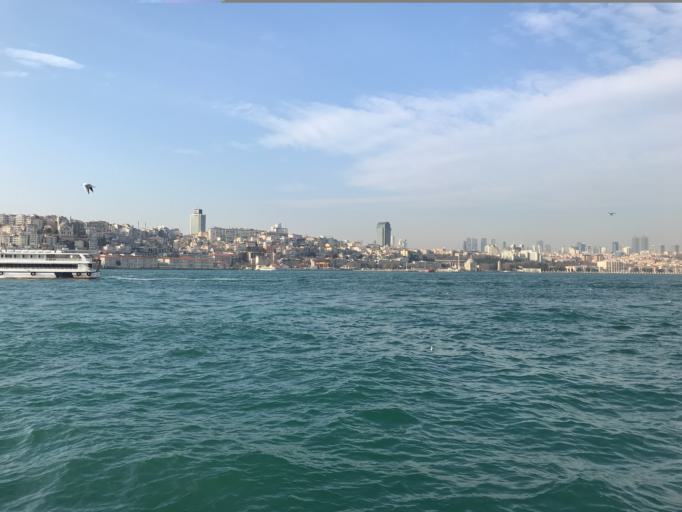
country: TR
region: Istanbul
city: Eminoenue
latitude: 41.0229
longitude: 28.9937
